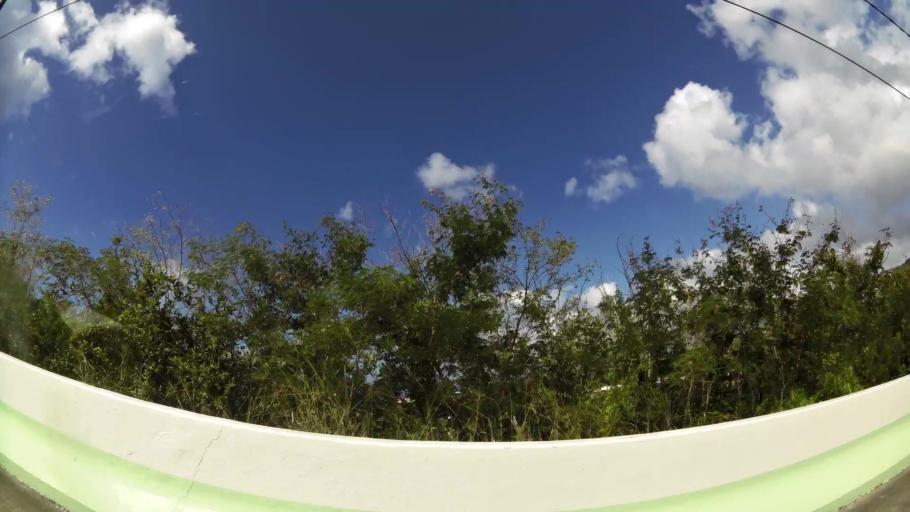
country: MQ
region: Martinique
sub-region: Martinique
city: Saint-Pierre
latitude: 14.6949
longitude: -61.1744
